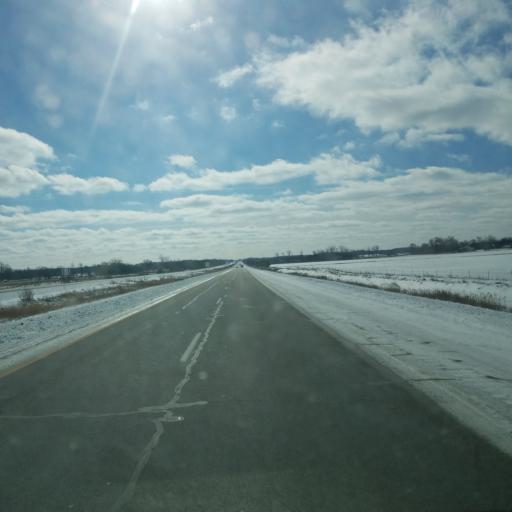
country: US
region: Michigan
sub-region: Clinton County
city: Saint Johns
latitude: 42.9846
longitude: -84.5190
